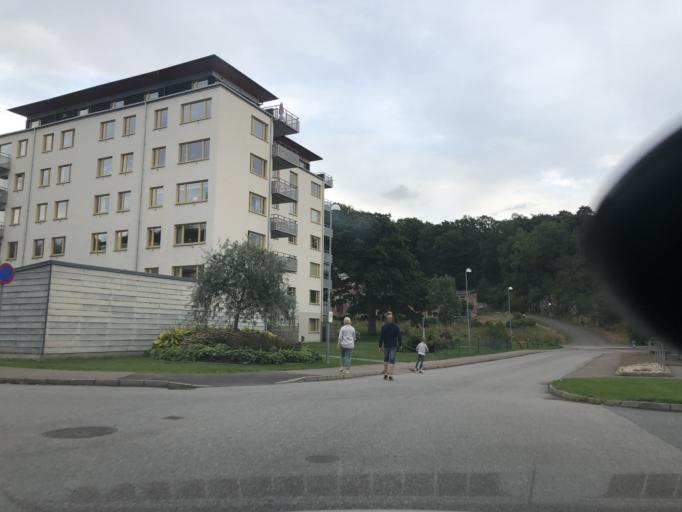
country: SE
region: Vaestra Goetaland
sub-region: Goteborg
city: Goeteborg
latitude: 57.7500
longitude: 11.9544
